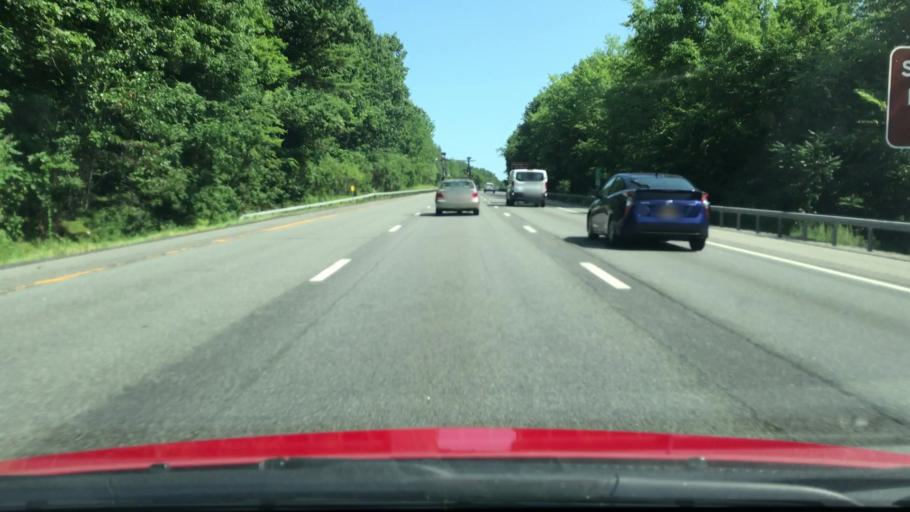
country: US
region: New York
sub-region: Saratoga County
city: Ballston Spa
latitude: 43.0044
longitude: -73.8019
